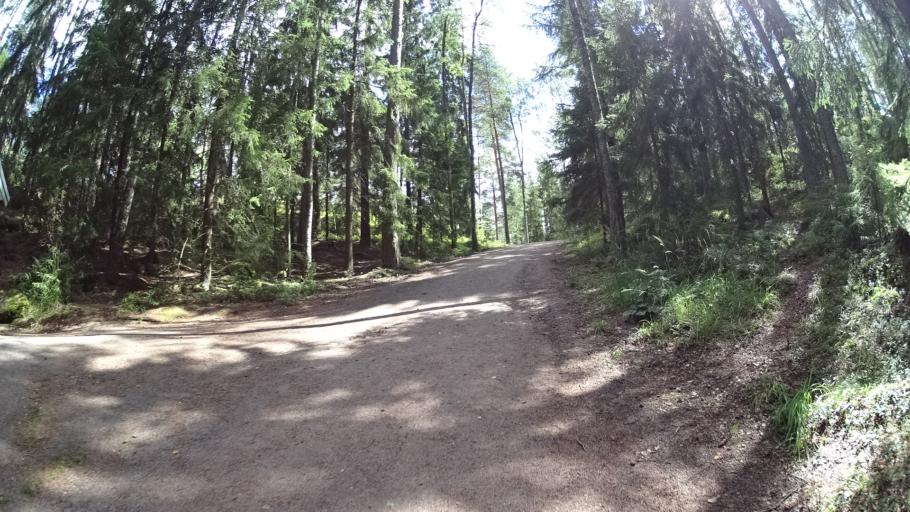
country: FI
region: Uusimaa
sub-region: Helsinki
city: Espoo
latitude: 60.3227
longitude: 24.6649
